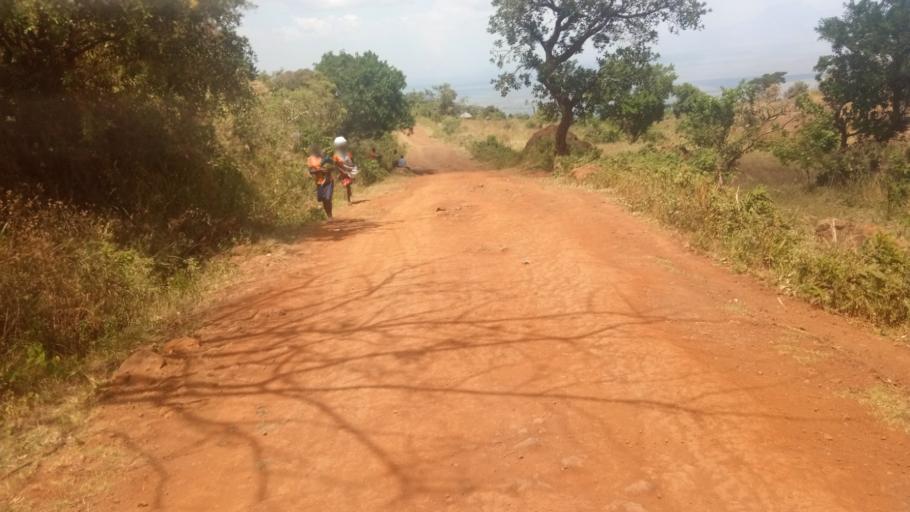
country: UG
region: Eastern Region
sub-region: Kween District
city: Binyin
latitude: 1.4330
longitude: 34.4930
